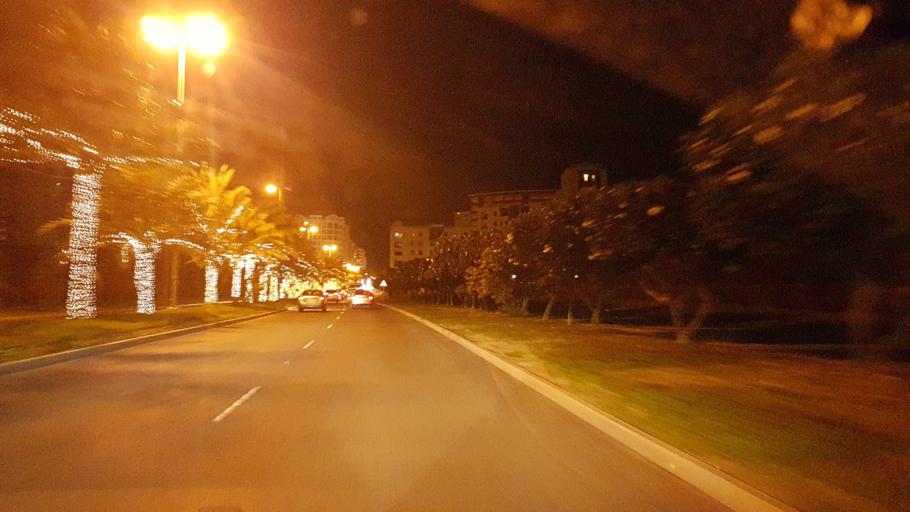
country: BH
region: Muharraq
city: Al Hadd
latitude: 26.2819
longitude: 50.6648
